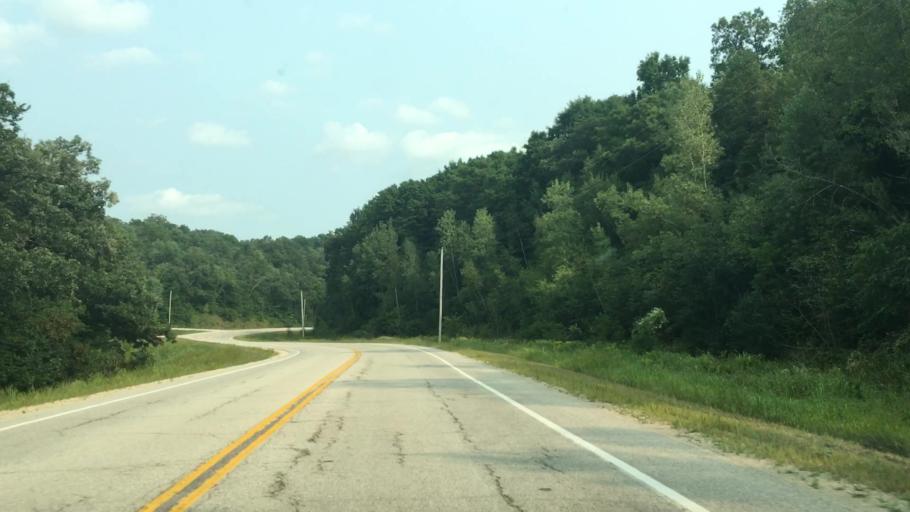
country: US
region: Minnesota
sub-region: Fillmore County
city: Preston
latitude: 43.7010
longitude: -91.9686
